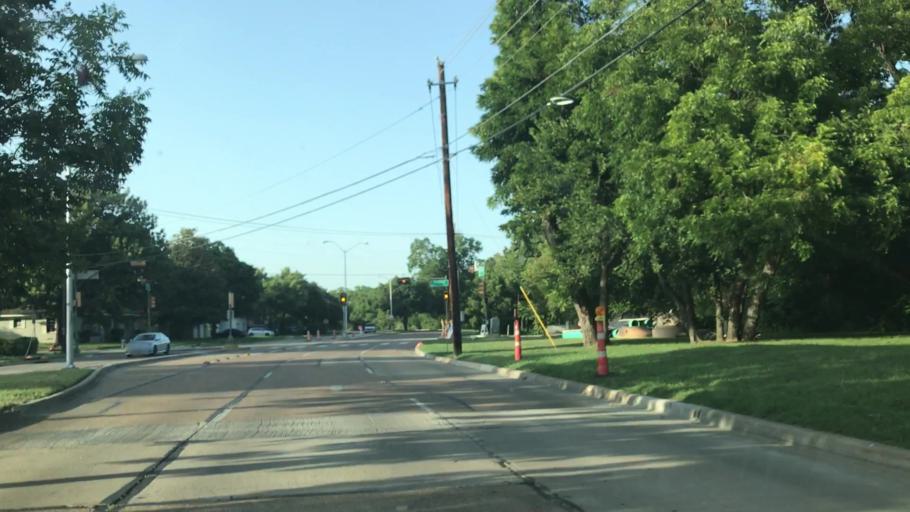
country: US
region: Texas
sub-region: Dallas County
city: Highland Park
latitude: 32.8442
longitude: -96.7055
